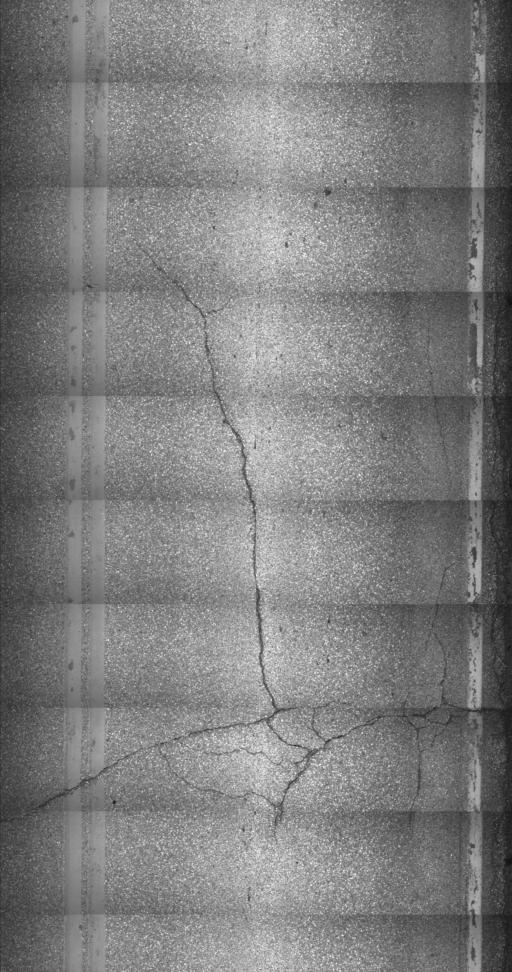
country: US
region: Vermont
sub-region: Franklin County
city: Enosburg Falls
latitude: 44.9908
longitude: -72.8140
